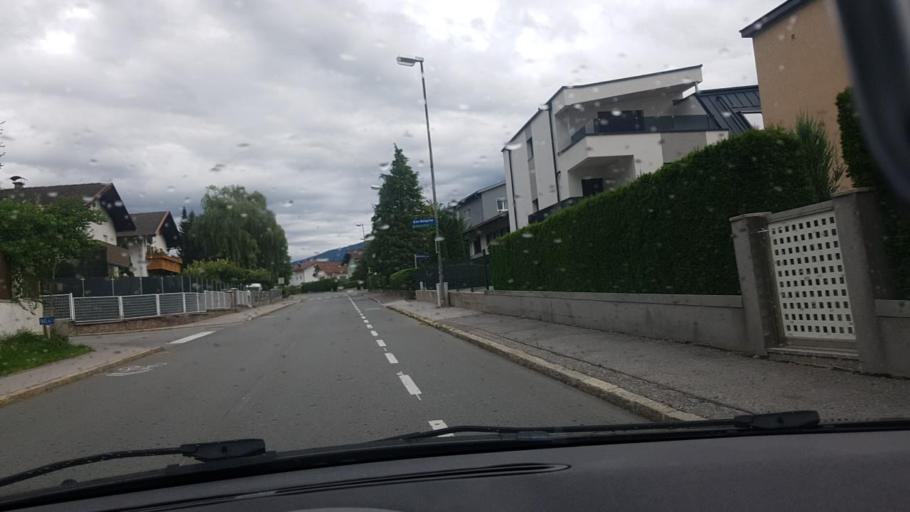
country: AT
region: Tyrol
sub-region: Politischer Bezirk Innsbruck Land
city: Zirl
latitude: 47.2758
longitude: 11.2343
